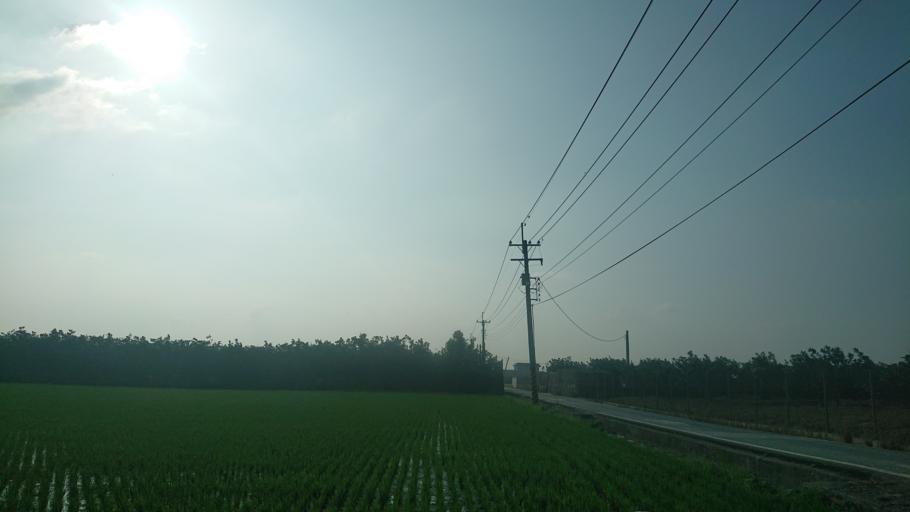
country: TW
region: Taiwan
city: Xinying
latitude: 23.1999
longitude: 120.2714
